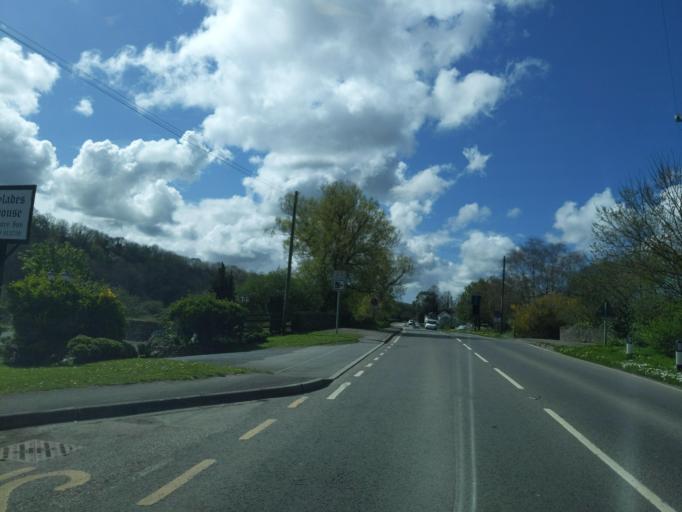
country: GB
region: England
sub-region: Cornwall
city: Wadebridge
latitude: 50.5090
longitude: -4.8065
